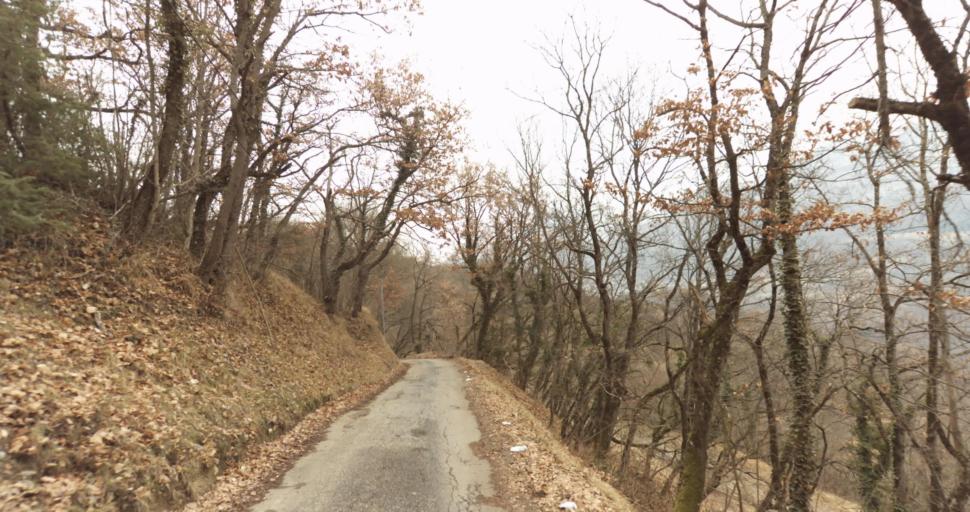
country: FR
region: Rhone-Alpes
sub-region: Departement de l'Isere
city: Saint-Georges-de-Commiers
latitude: 45.0189
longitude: 5.6854
